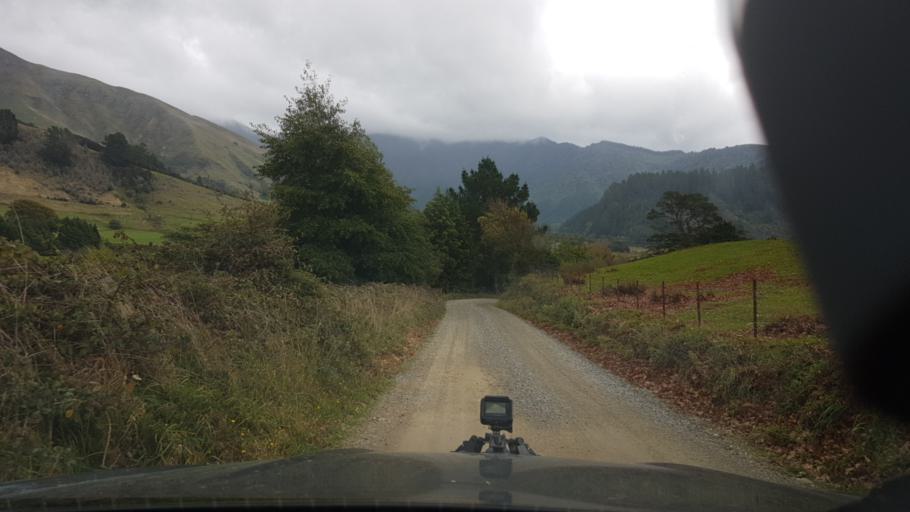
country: NZ
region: Marlborough
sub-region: Marlborough District
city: Blenheim
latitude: -41.3724
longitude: 173.7639
